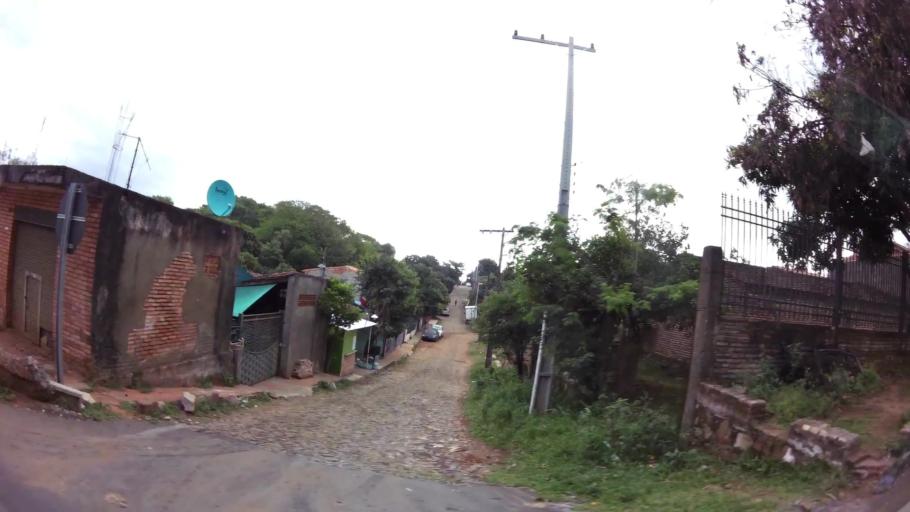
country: PY
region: Central
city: Fernando de la Mora
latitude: -25.3445
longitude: -57.5601
